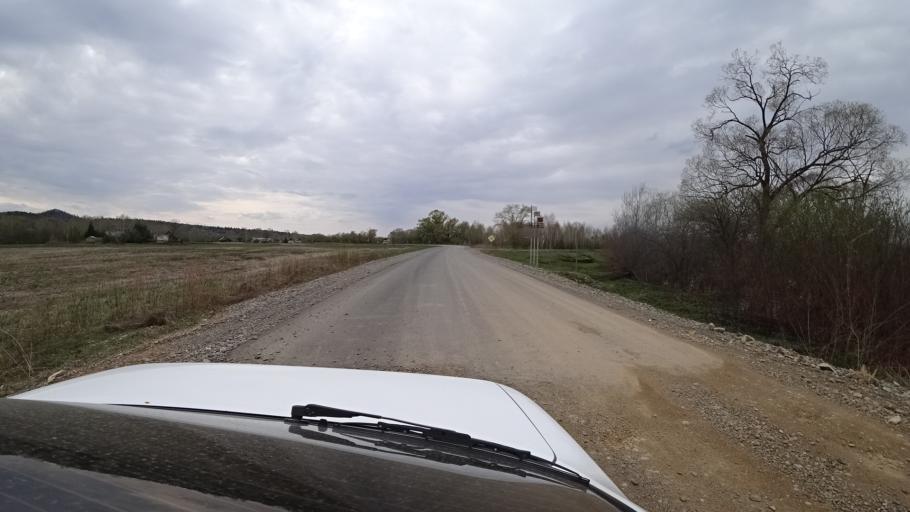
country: RU
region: Primorskiy
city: Novopokrovka
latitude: 45.4915
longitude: 134.4547
